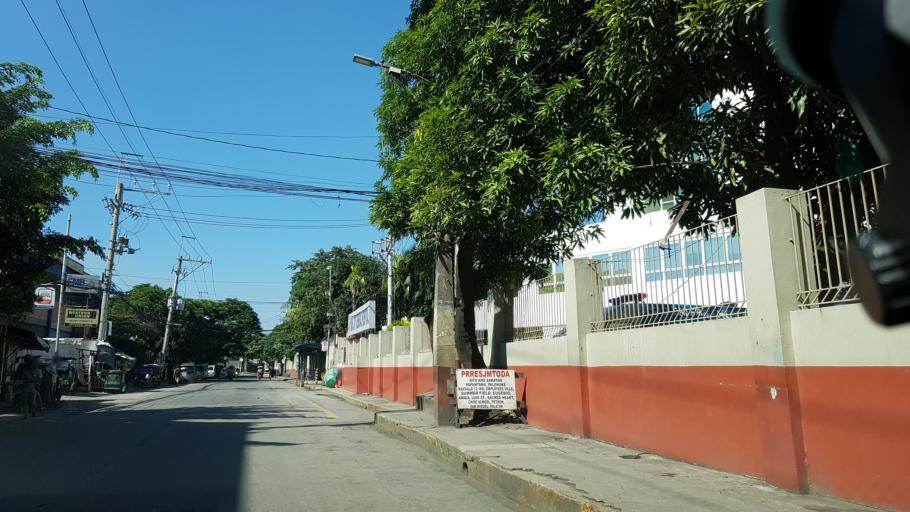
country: PH
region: Calabarzon
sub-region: Province of Rizal
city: Cainta
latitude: 14.5724
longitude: 121.0998
